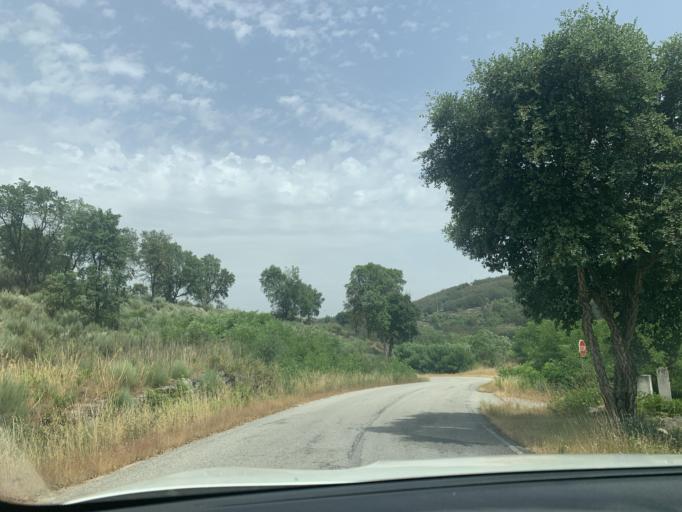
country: PT
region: Guarda
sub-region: Fornos de Algodres
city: Fornos de Algodres
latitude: 40.5692
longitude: -7.5965
